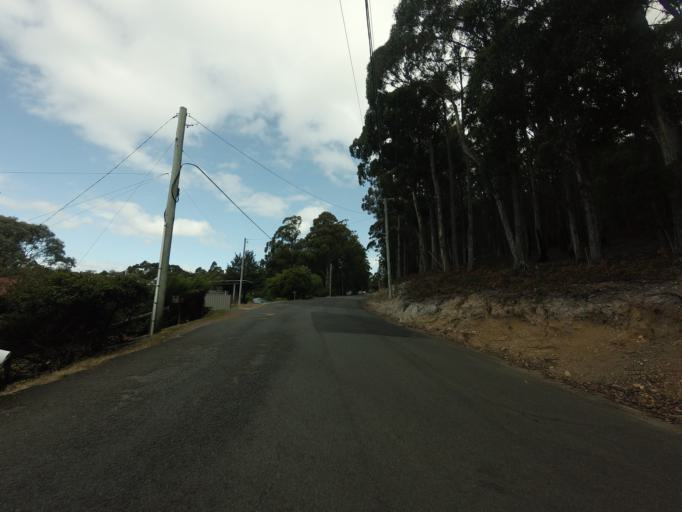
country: AU
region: Tasmania
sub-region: Hobart
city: Dynnyrne
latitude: -42.9086
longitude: 147.2666
